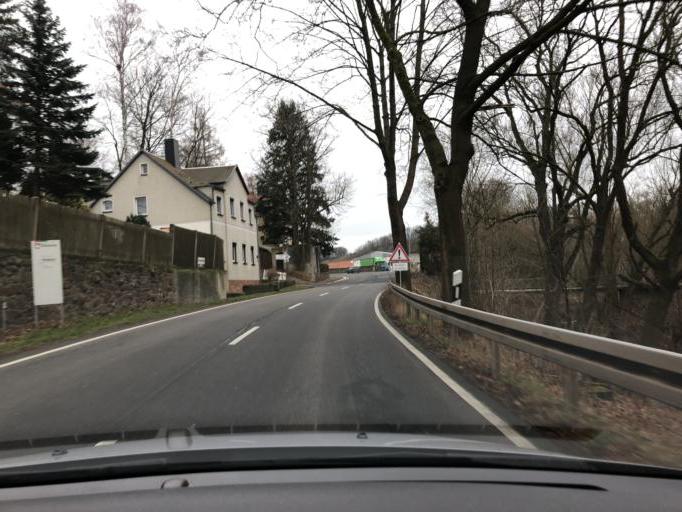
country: DE
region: Saxony
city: Rosswein
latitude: 51.0677
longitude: 13.1751
